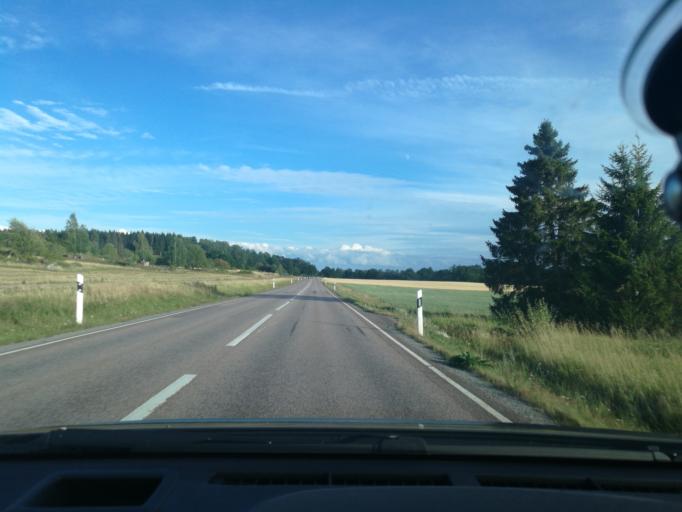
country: SE
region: Vaestmanland
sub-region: Vasteras
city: Skultuna
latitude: 59.6819
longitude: 16.4628
